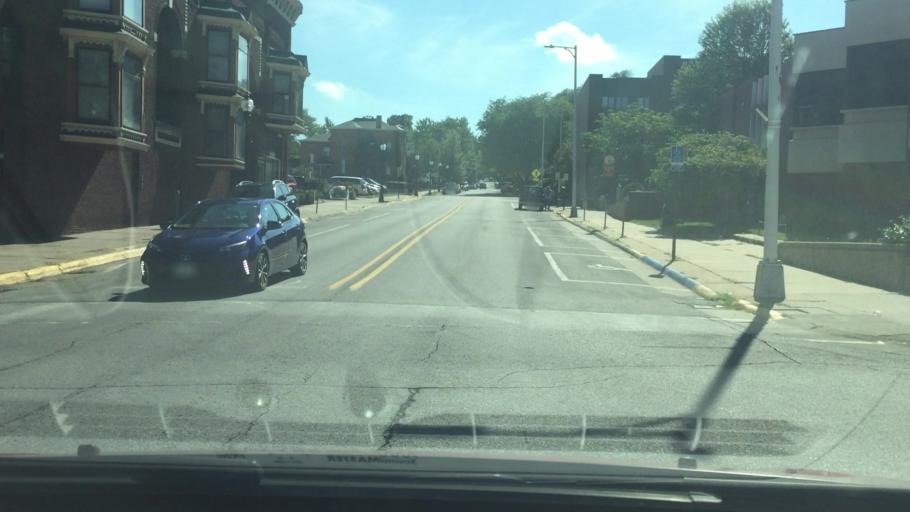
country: US
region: Iowa
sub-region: Muscatine County
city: Muscatine
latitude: 41.4221
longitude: -91.0465
